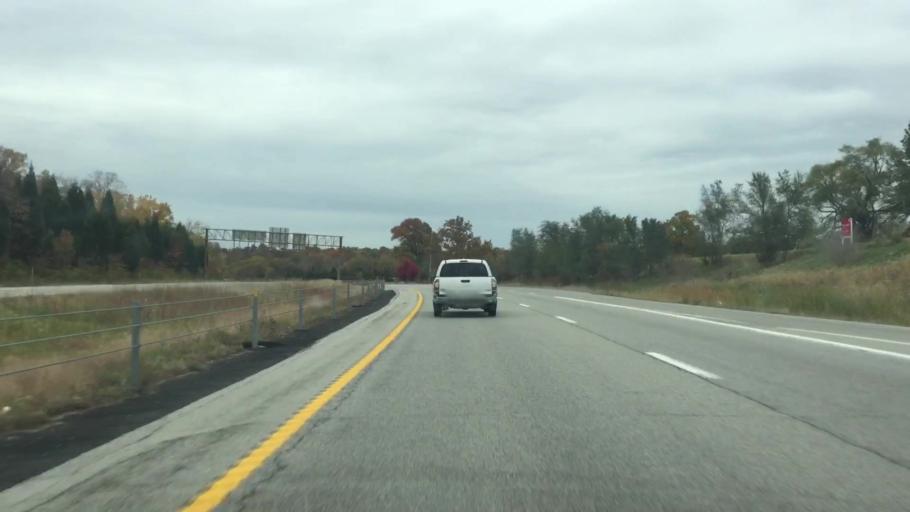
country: US
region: Missouri
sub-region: Jackson County
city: Lees Summit
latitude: 38.9465
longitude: -94.4096
